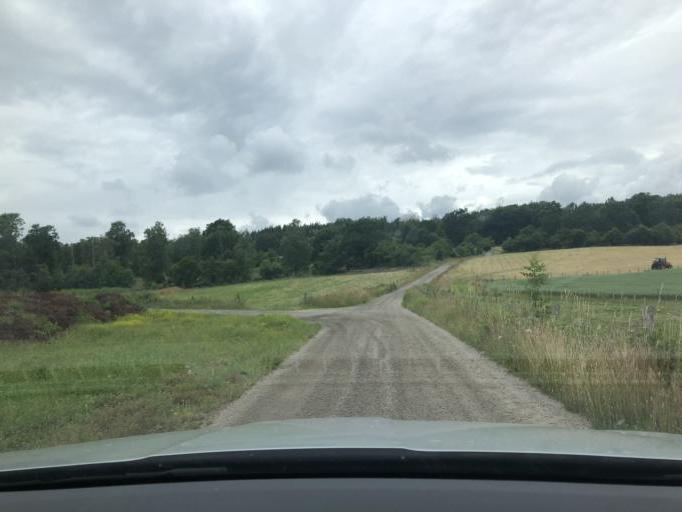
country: SE
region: Blekinge
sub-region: Solvesborgs Kommun
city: Soelvesborg
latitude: 56.1546
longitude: 14.5953
